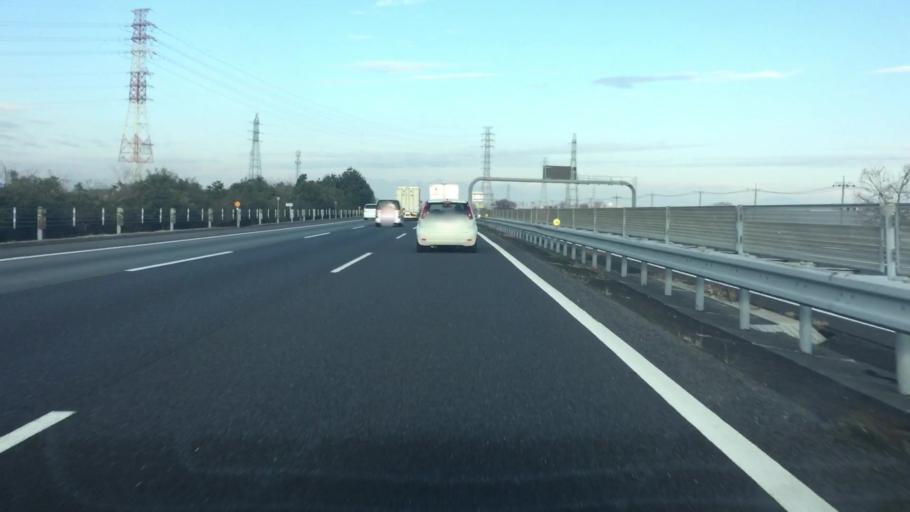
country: JP
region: Saitama
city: Honjo
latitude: 36.2224
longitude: 139.1611
